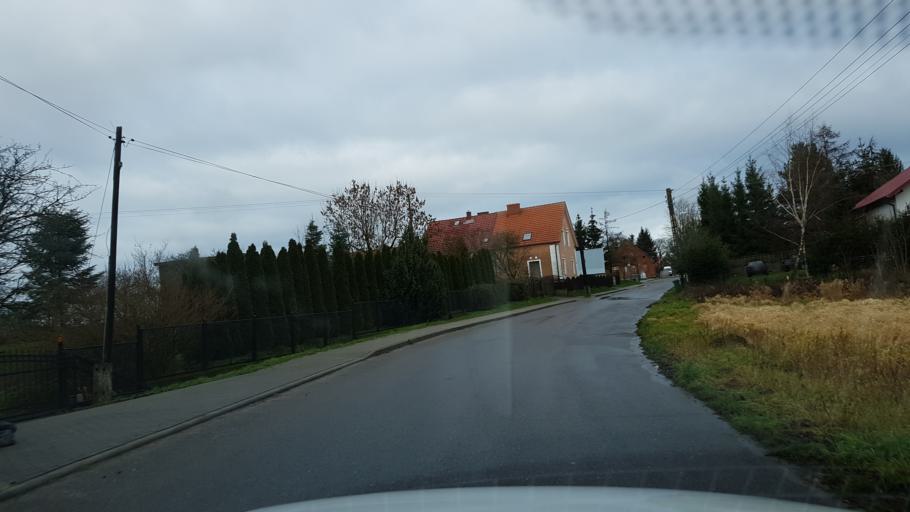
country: PL
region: West Pomeranian Voivodeship
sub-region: Powiat slawienski
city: Slawno
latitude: 54.5123
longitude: 16.6540
